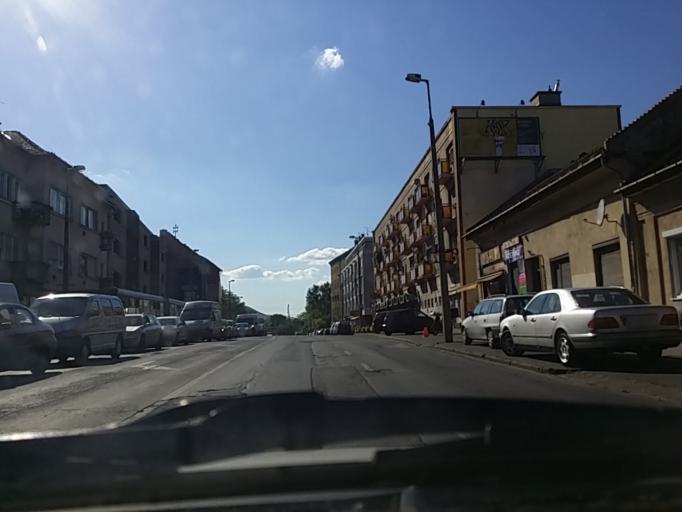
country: HU
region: Budapest
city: Budapest IV. keruelet
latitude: 47.5607
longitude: 19.0824
